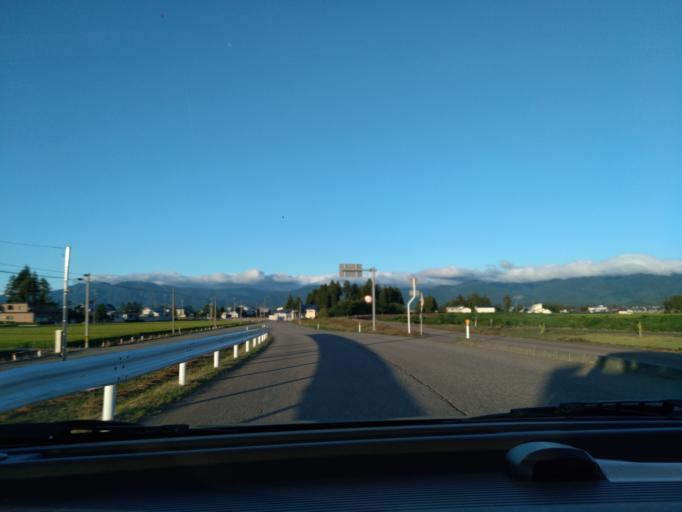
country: JP
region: Akita
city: Omagari
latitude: 39.4818
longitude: 140.5283
